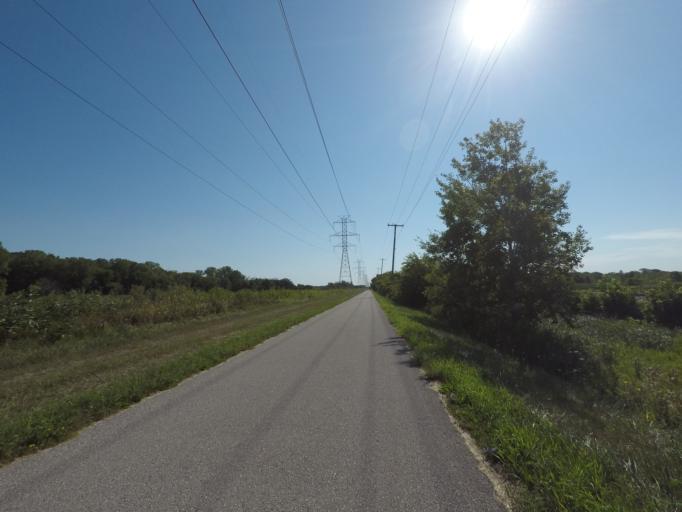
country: US
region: Wisconsin
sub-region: Waukesha County
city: New Berlin
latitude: 43.0100
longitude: -88.1578
